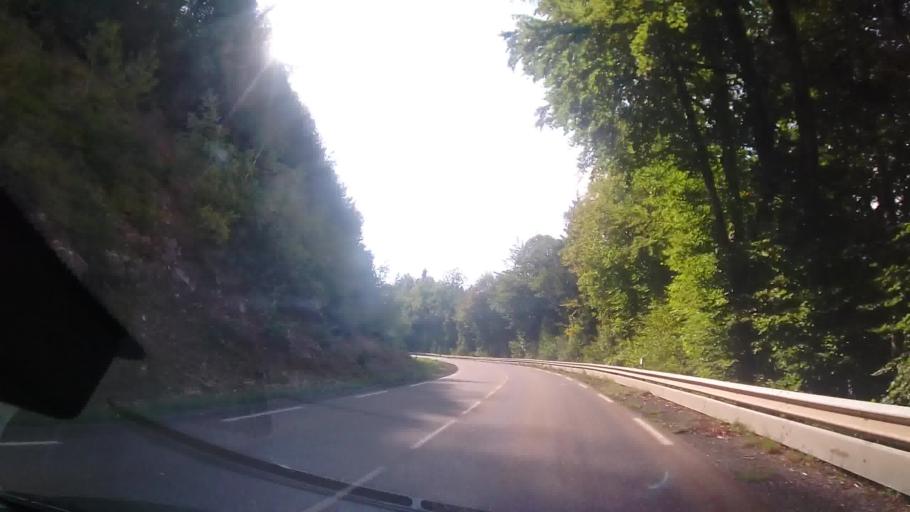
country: FR
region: Franche-Comte
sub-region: Departement du Jura
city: Clairvaux-les-Lacs
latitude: 46.5847
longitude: 5.8241
